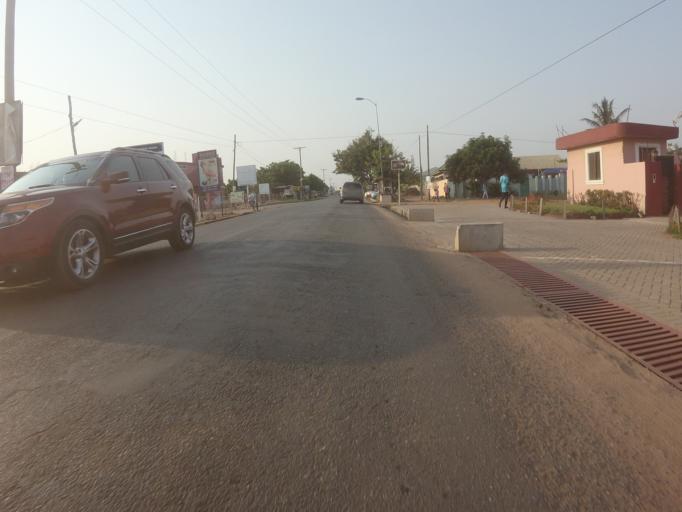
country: GH
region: Greater Accra
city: Nungua
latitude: 5.6186
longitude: -0.0538
